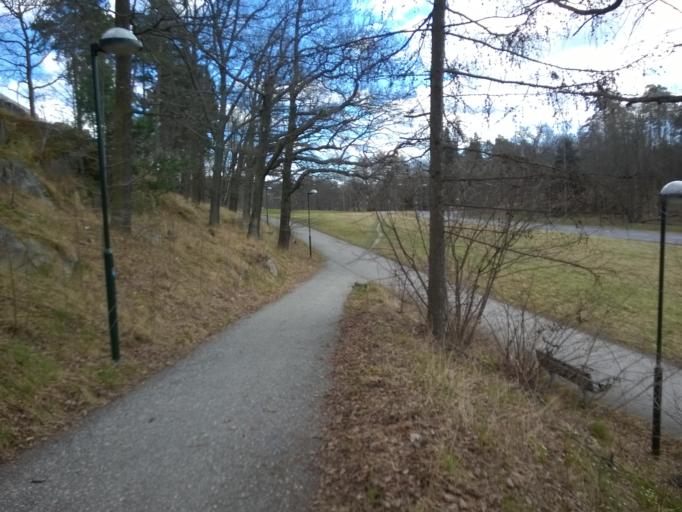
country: SE
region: Stockholm
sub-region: Danderyds Kommun
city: Djursholm
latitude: 59.3693
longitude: 18.0634
